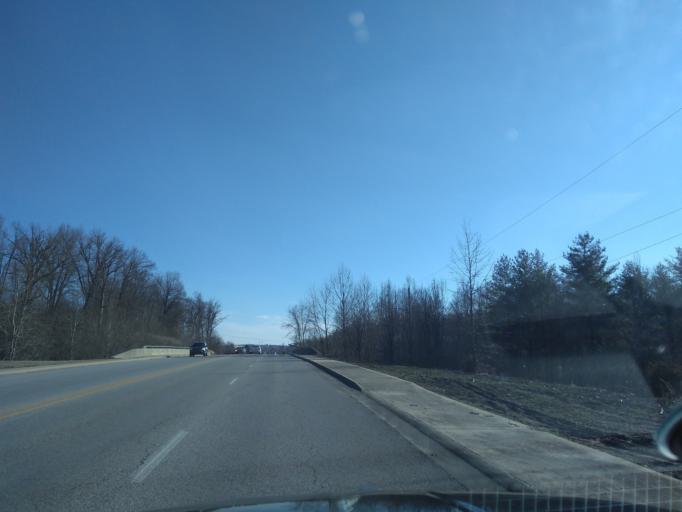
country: US
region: Arkansas
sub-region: Washington County
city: Johnson
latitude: 36.1288
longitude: -94.1631
